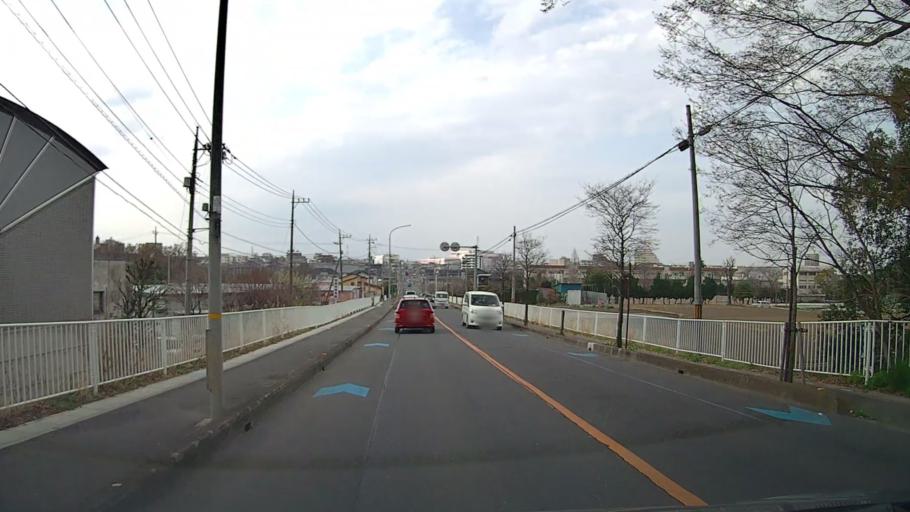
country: JP
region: Saitama
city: Asaka
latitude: 35.8127
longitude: 139.5981
